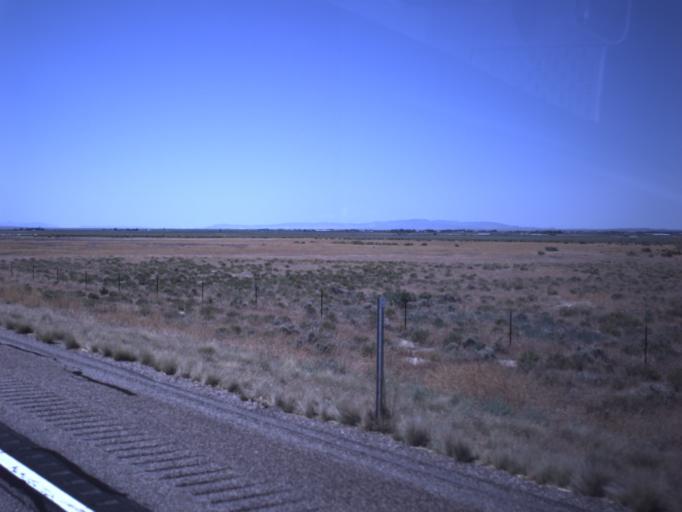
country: US
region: Utah
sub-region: Millard County
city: Delta
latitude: 39.3609
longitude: -112.4965
